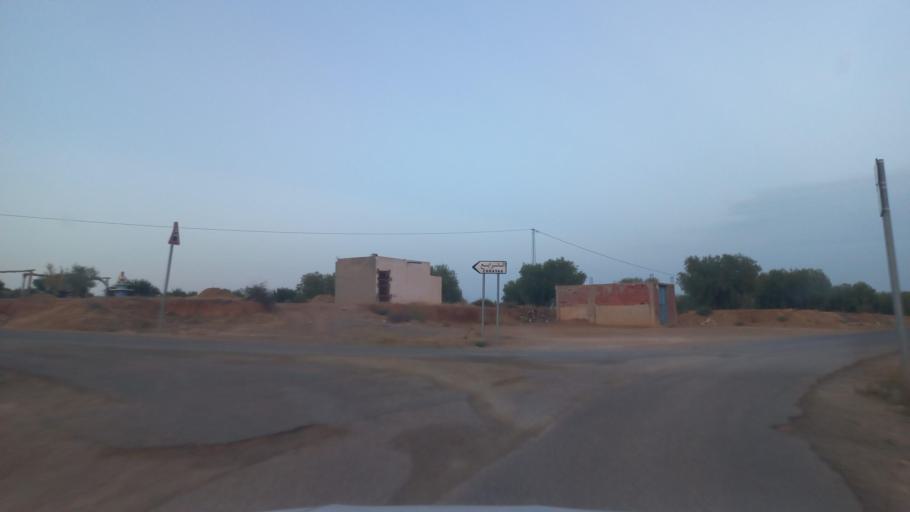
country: TN
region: Al Qasrayn
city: Kasserine
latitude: 35.2240
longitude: 9.0613
